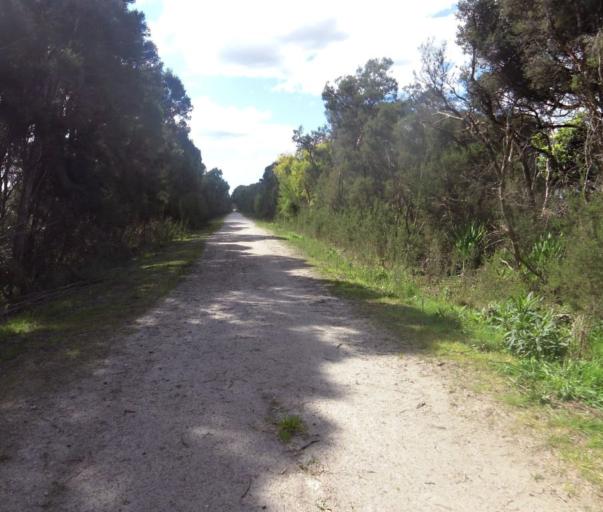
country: AU
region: Victoria
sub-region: Bass Coast
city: North Wonthaggi
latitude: -38.6429
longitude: 146.0321
